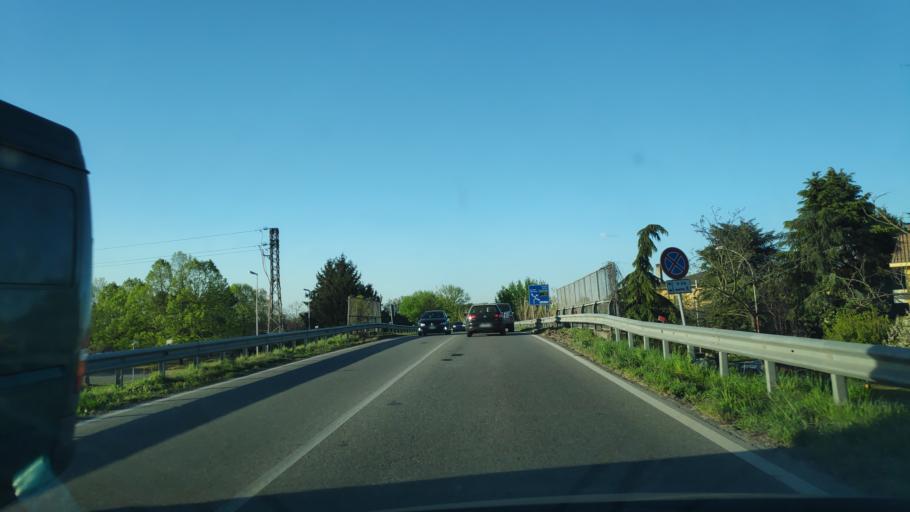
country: IT
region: Lombardy
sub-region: Citta metropolitana di Milano
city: Pieve Emanuele
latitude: 45.3545
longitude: 9.1995
